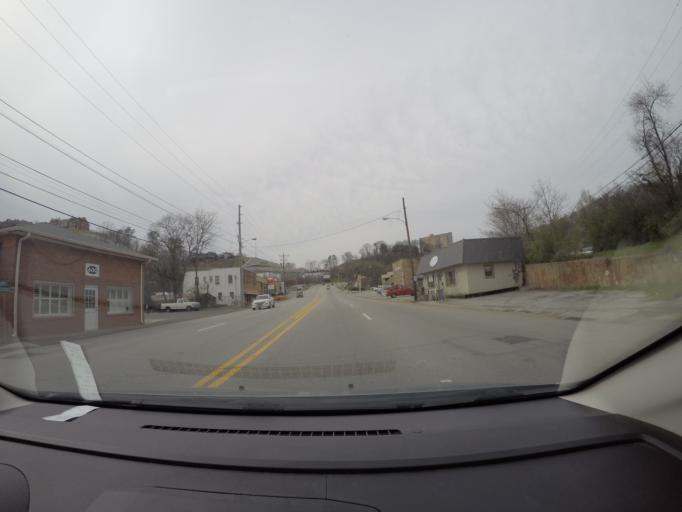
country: US
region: Tennessee
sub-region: Hamilton County
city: Chattanooga
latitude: 35.0689
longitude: -85.3171
